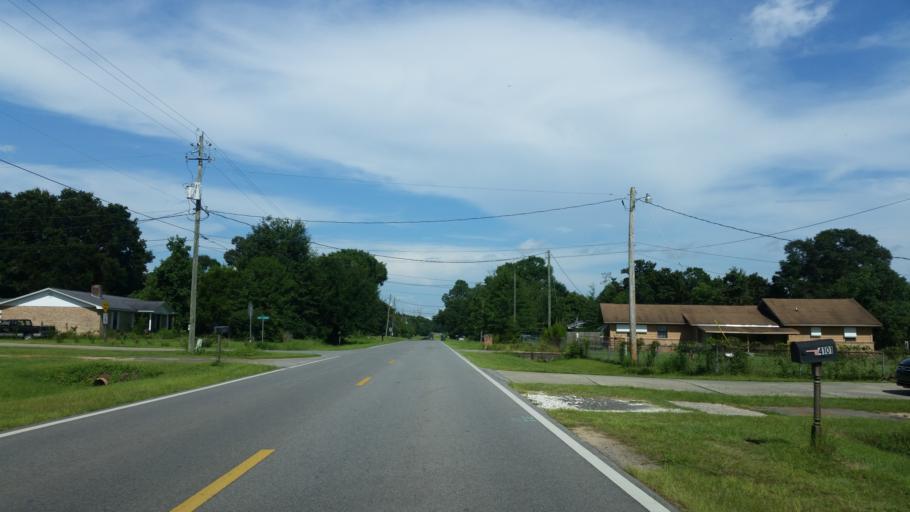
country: US
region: Florida
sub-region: Santa Rosa County
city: Pace
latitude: 30.5896
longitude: -87.1529
